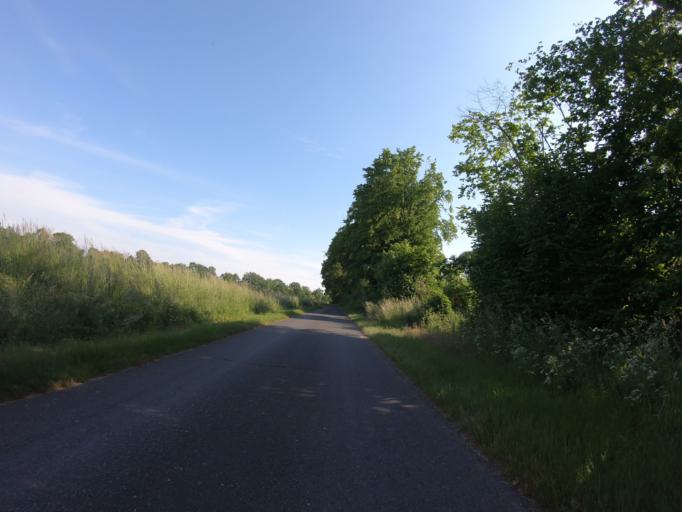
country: DE
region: Lower Saxony
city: Wasbuttel
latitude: 52.3953
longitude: 10.6009
